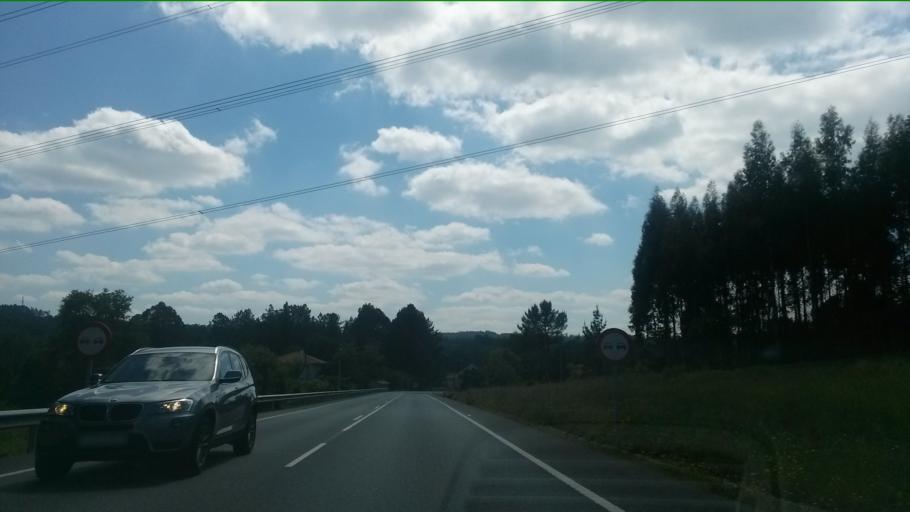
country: ES
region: Galicia
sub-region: Provincia da Coruna
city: Touro
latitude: 42.9518
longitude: -8.3289
